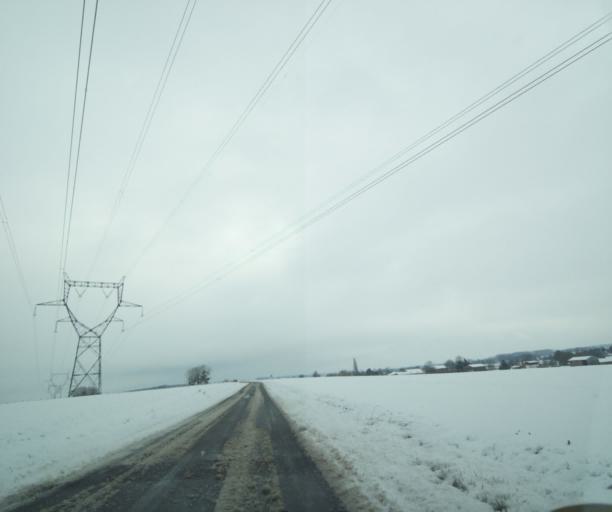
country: FR
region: Champagne-Ardenne
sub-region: Departement de la Haute-Marne
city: Montier-en-Der
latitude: 48.5084
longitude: 4.7178
